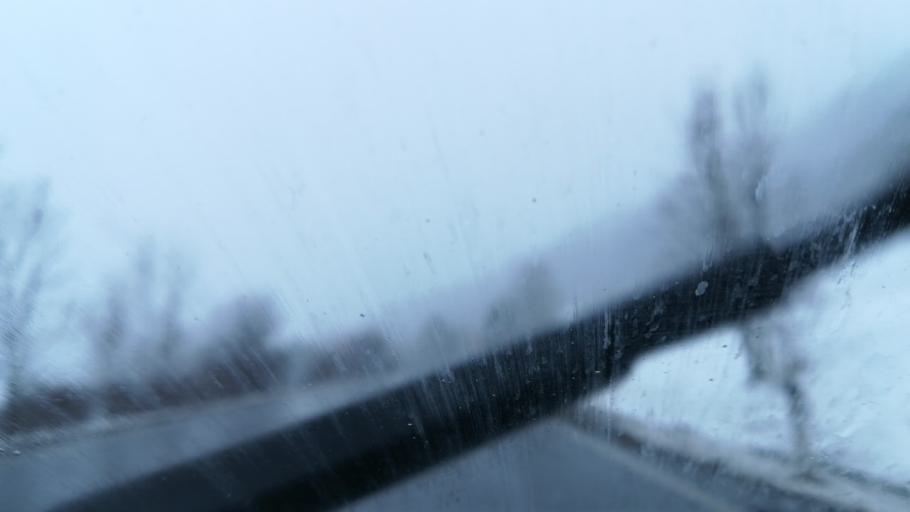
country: AT
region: Styria
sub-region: Politischer Bezirk Murtal
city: Poels
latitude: 47.2017
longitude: 14.5879
